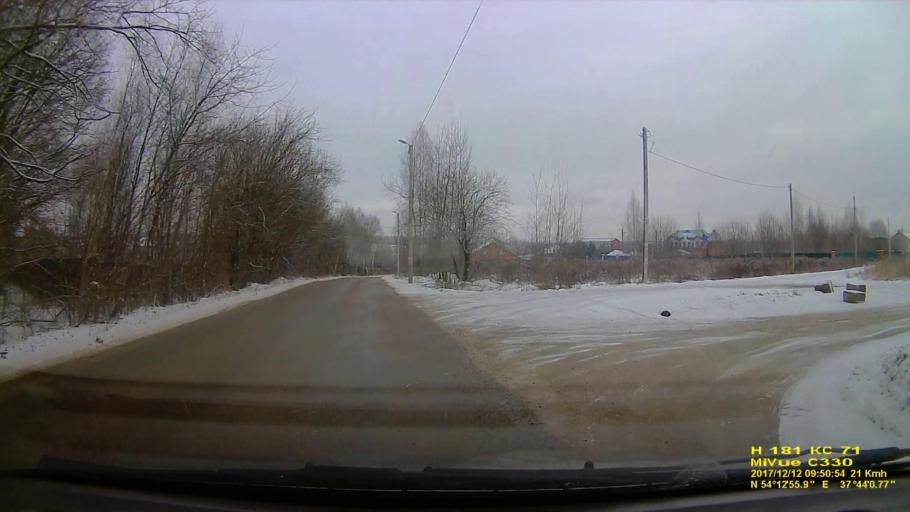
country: RU
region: Tula
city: Tula
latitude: 54.2155
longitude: 37.7336
